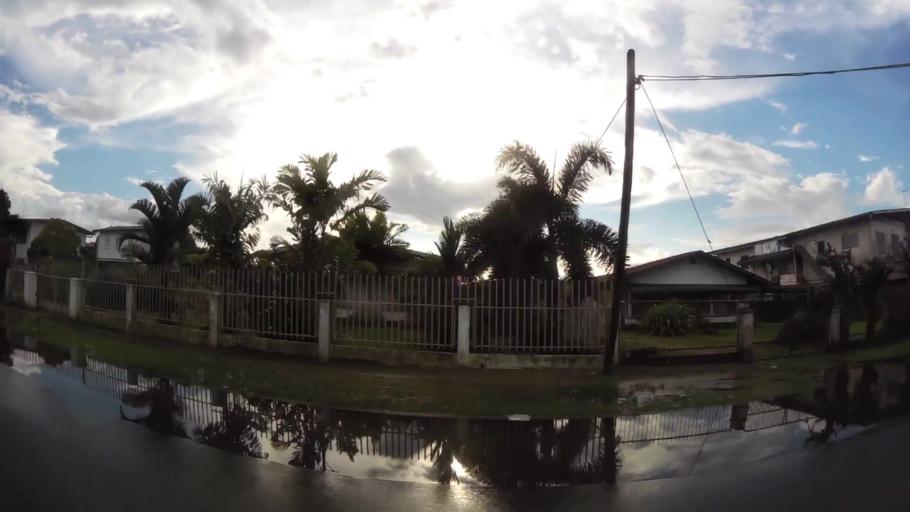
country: SR
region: Paramaribo
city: Paramaribo
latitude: 5.8263
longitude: -55.1814
